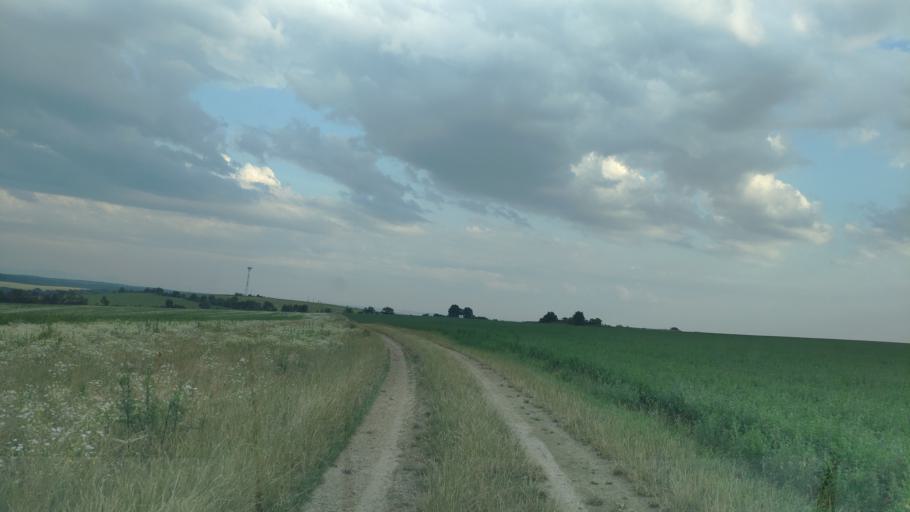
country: SK
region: Kosicky
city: Moldava nad Bodvou
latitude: 48.6905
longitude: 20.9895
